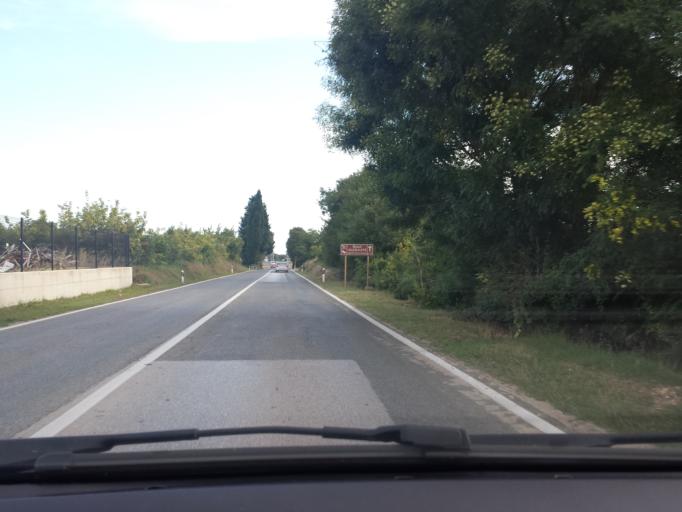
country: HR
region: Istarska
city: Galizana
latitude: 44.9075
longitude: 13.8473
